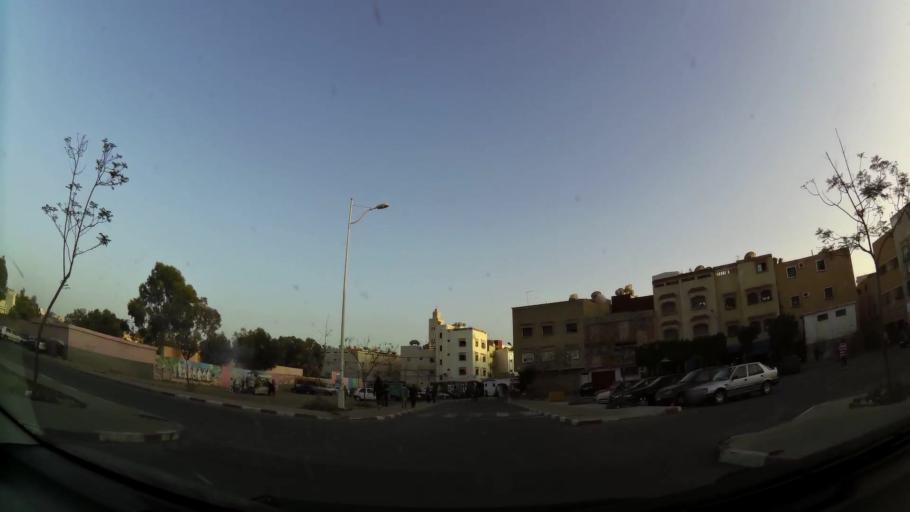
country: MA
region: Oued ed Dahab-Lagouira
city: Dakhla
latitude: 30.3894
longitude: -9.5666
